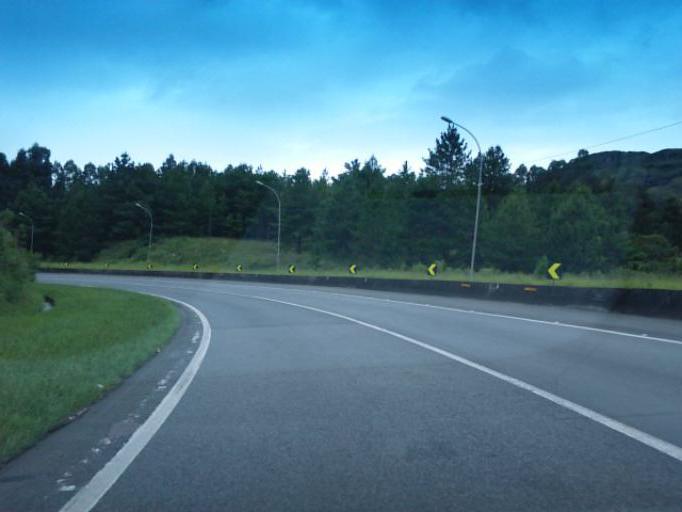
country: BR
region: Parana
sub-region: Campina Grande Do Sul
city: Campina Grande do Sul
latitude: -25.1152
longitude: -48.8475
